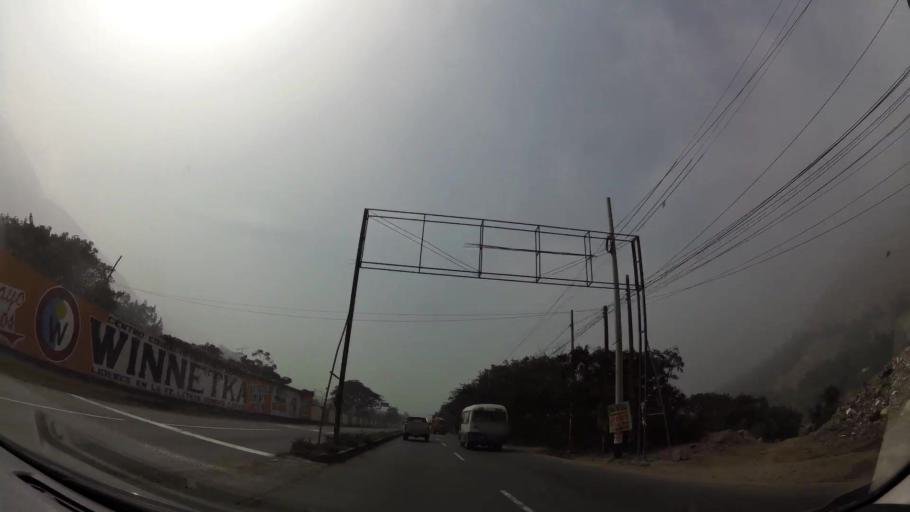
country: PE
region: Lima
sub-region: Lima
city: Chosica
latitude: -11.9611
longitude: -76.7374
